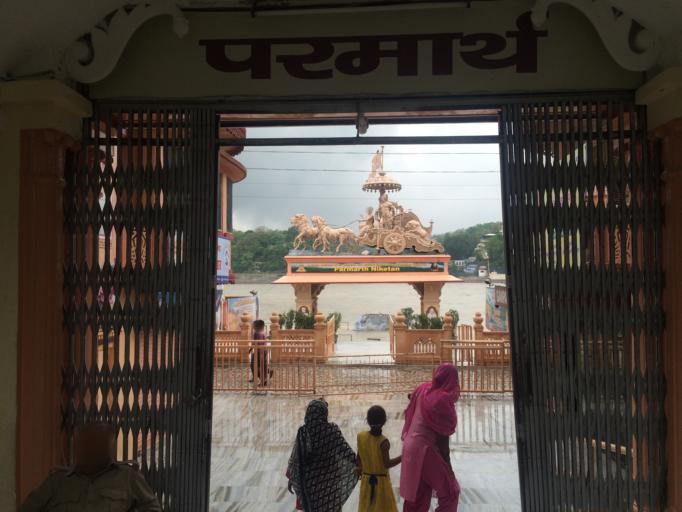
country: IN
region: Uttarakhand
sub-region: Dehradun
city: Rishikesh
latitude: 30.1193
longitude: 78.3120
